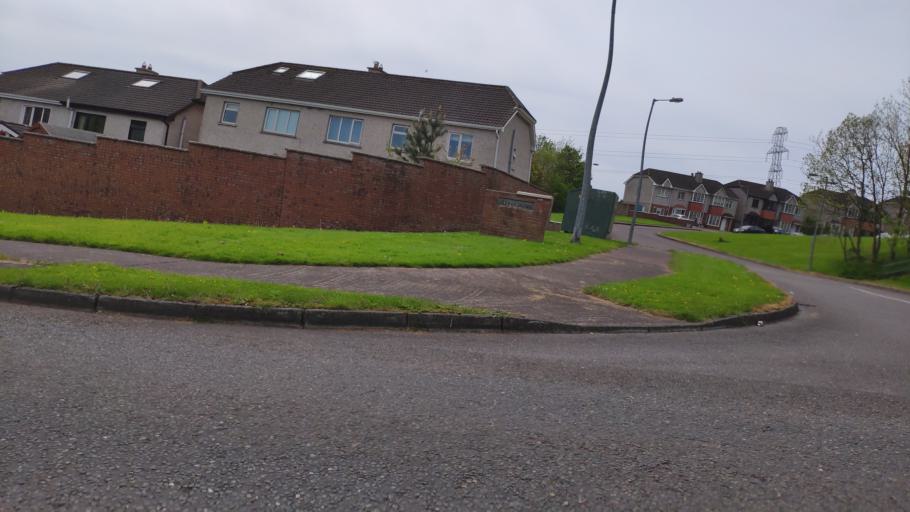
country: IE
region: Munster
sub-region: County Cork
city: Cork
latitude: 51.9246
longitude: -8.4572
